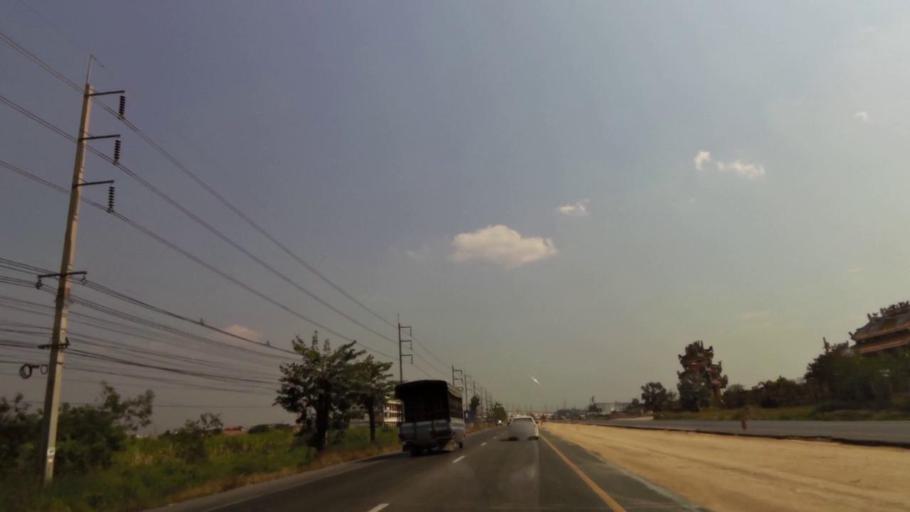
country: TH
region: Chon Buri
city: Ban Bueng
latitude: 13.2919
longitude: 101.1690
